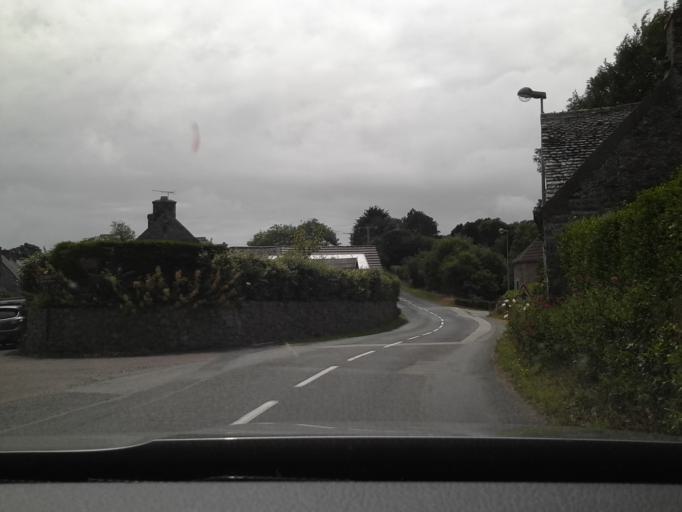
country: FR
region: Lower Normandy
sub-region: Departement de la Manche
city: Urville-Nacqueville
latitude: 49.6762
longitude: -1.7801
